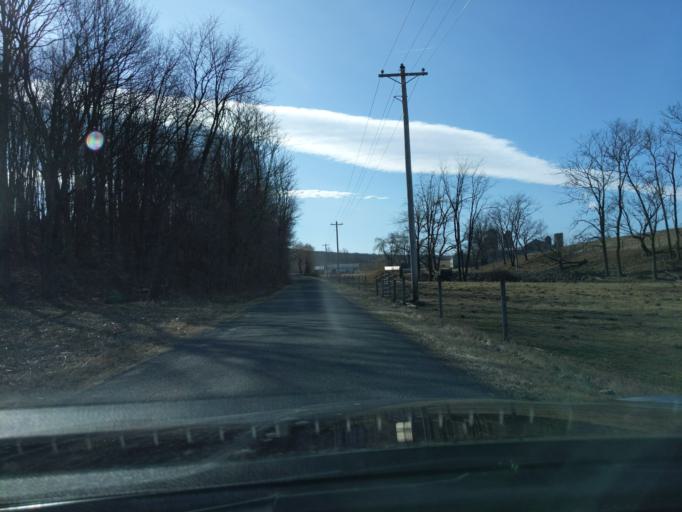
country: US
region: Pennsylvania
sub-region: Blair County
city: Martinsburg
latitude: 40.3772
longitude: -78.2769
